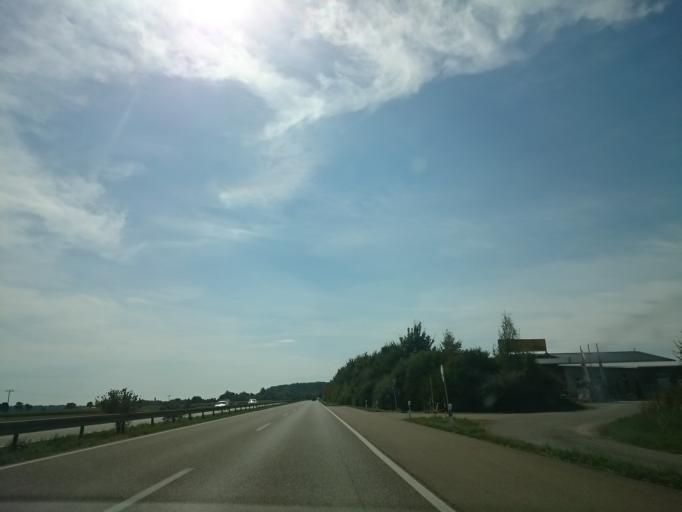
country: DE
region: Bavaria
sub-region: Swabia
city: Nordendorf
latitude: 48.6014
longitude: 10.8390
